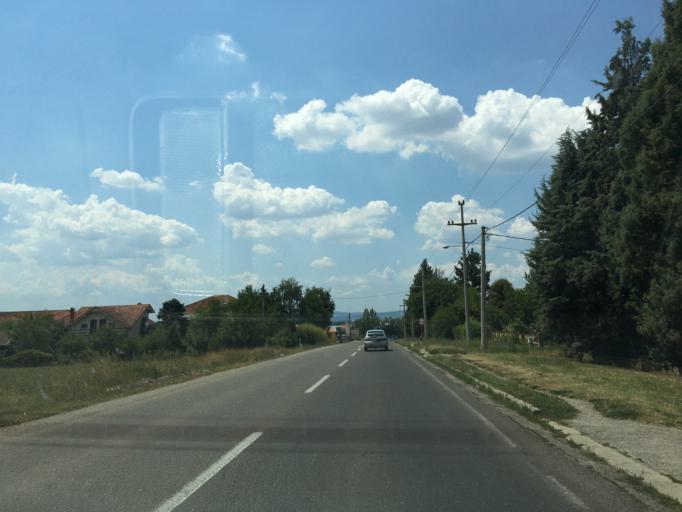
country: RS
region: Central Serbia
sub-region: Belgrade
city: Mladenovac
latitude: 44.4078
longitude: 20.6747
